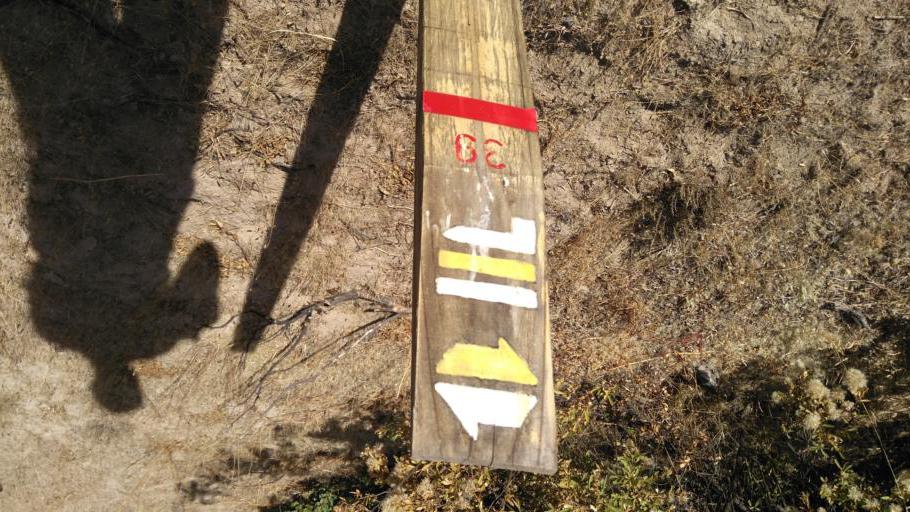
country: CL
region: Santiago Metropolitan
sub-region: Provincia de Cordillera
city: Puente Alto
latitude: -33.7213
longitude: -70.4542
